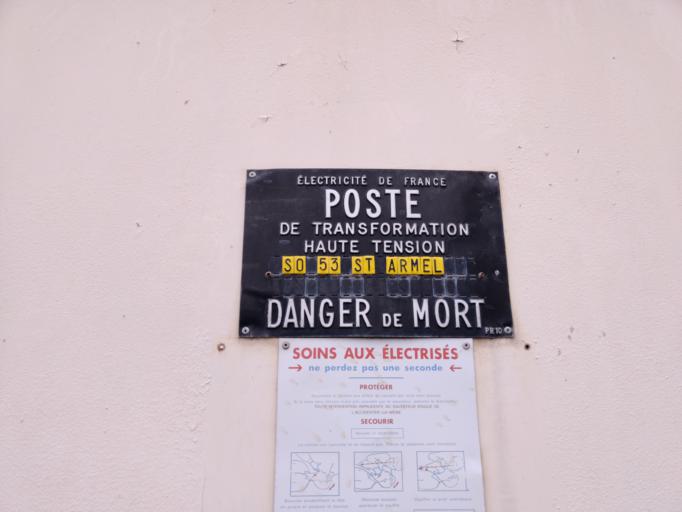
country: FR
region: Pays de la Loire
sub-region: Departement de la Vendee
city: Les Sables-d'Olonne
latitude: 46.5032
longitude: -1.7834
